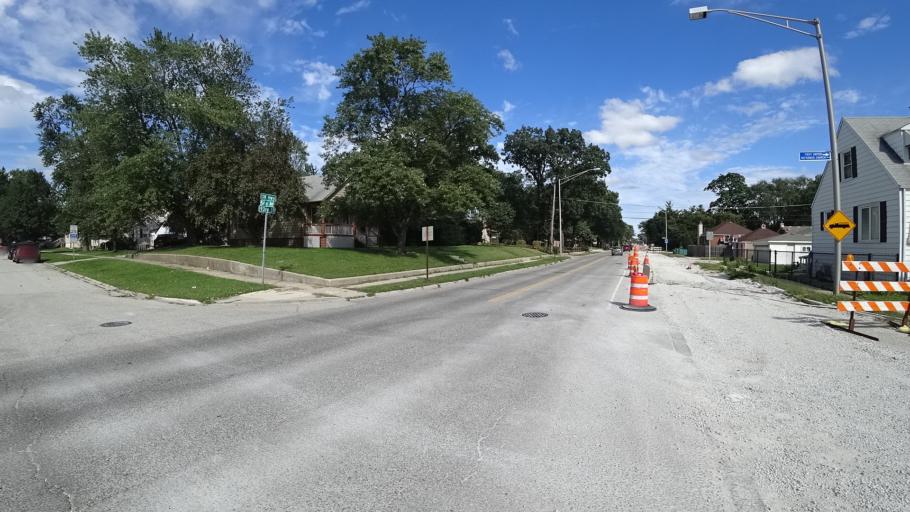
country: US
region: Illinois
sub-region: Cook County
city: Oak Lawn
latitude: 41.7234
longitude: -87.7555
